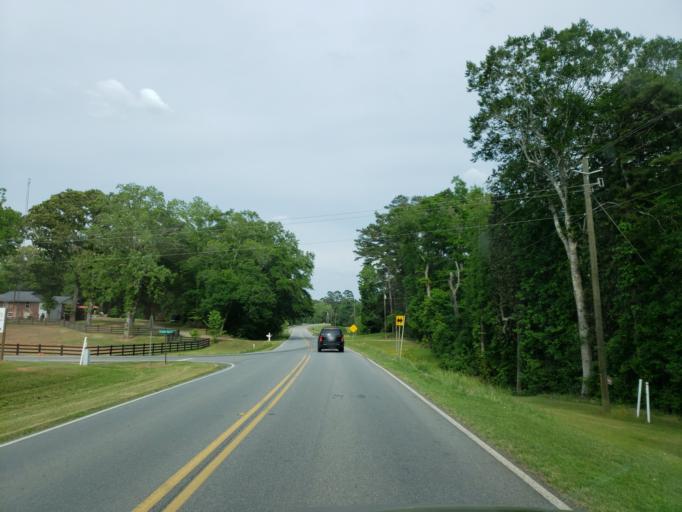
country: US
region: Georgia
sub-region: Dooly County
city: Vienna
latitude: 32.1109
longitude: -83.8395
